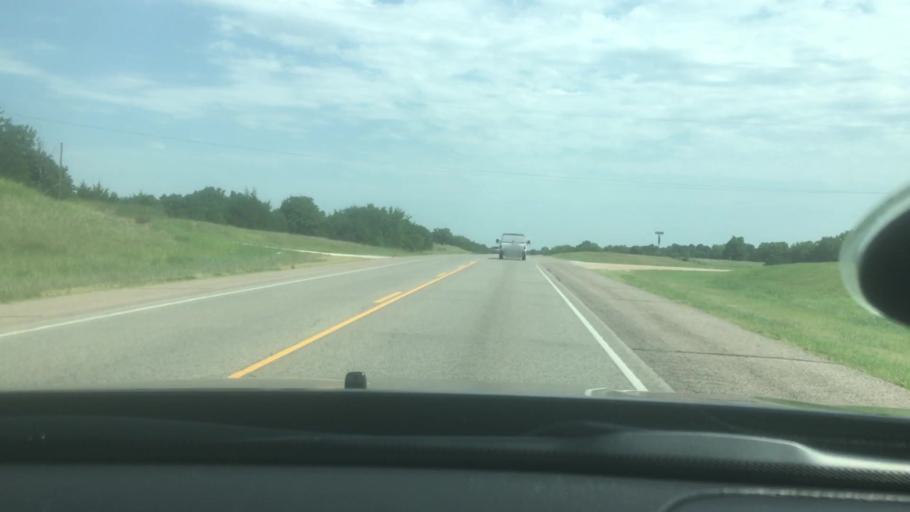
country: US
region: Oklahoma
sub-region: Seminole County
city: Maud
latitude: 35.0287
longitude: -96.9314
